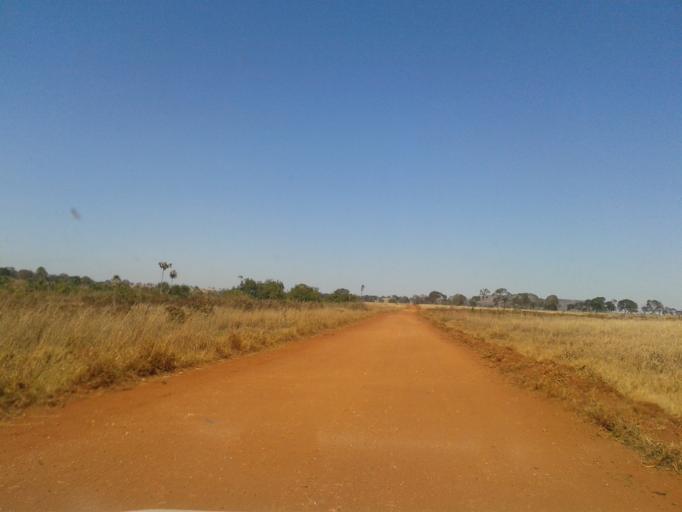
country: BR
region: Minas Gerais
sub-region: Santa Vitoria
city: Santa Vitoria
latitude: -19.1533
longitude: -50.1564
